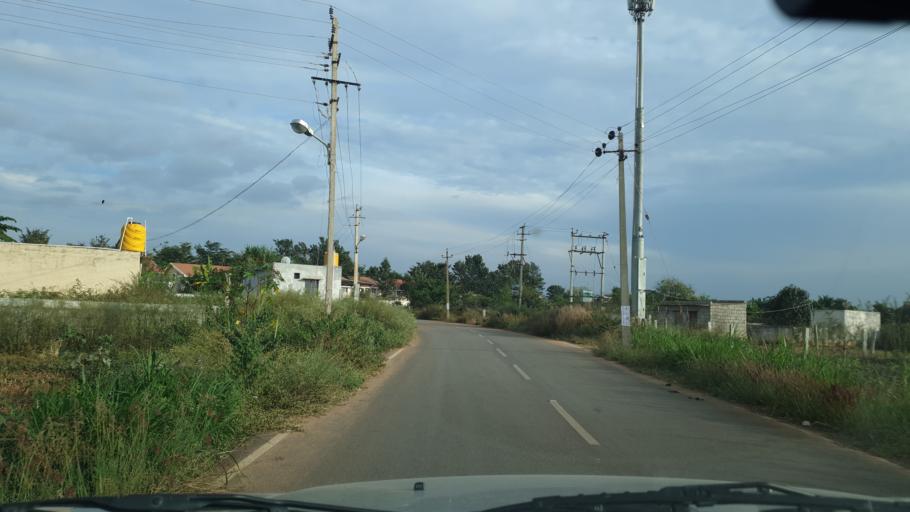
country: IN
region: Karnataka
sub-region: Bangalore Urban
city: Yelahanka
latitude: 13.1940
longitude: 77.6220
